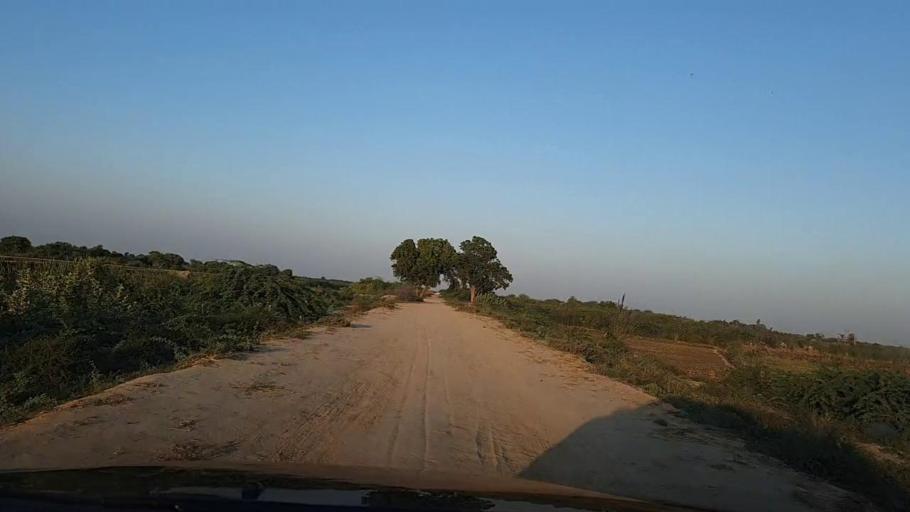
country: PK
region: Sindh
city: Thatta
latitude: 24.7186
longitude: 67.9406
